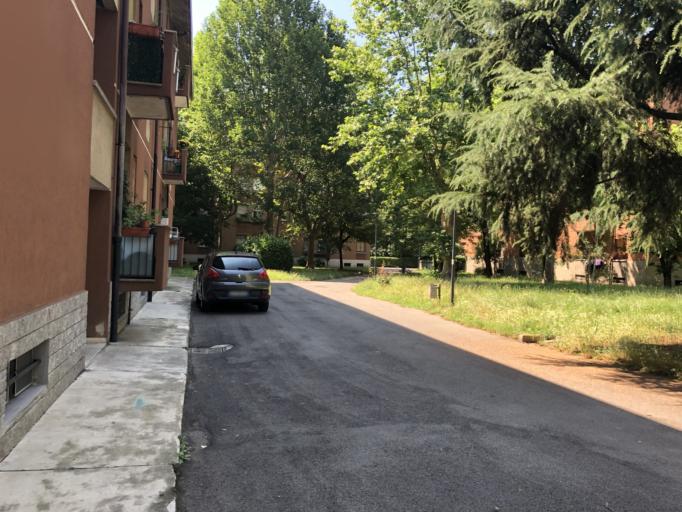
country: IT
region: Lombardy
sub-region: Citta metropolitana di Milano
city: Cormano
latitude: 45.5232
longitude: 9.1610
